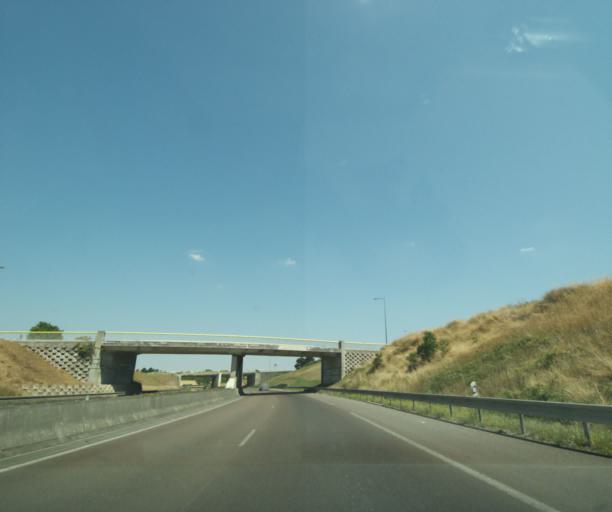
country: FR
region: Champagne-Ardenne
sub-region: Departement de la Marne
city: Saint-Memmie
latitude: 48.9617
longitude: 4.3908
